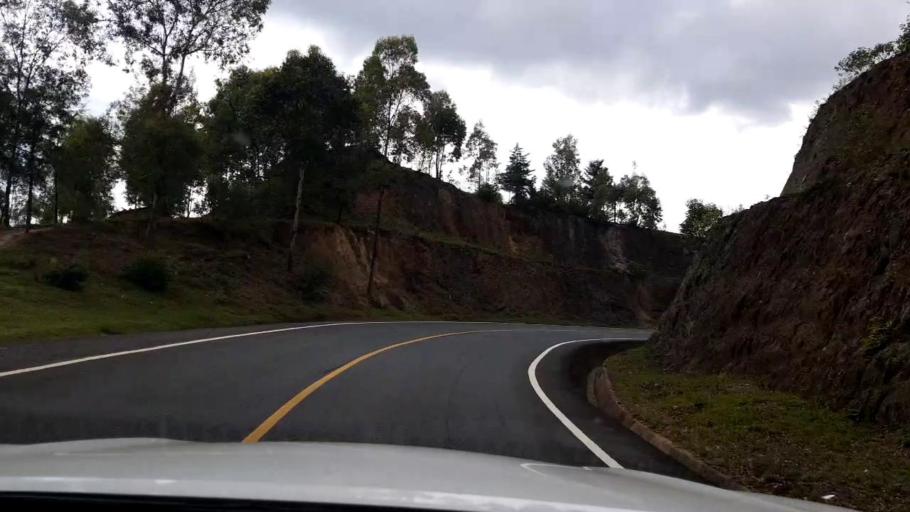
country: RW
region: Southern Province
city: Gitarama
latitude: -2.0287
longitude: 29.7171
